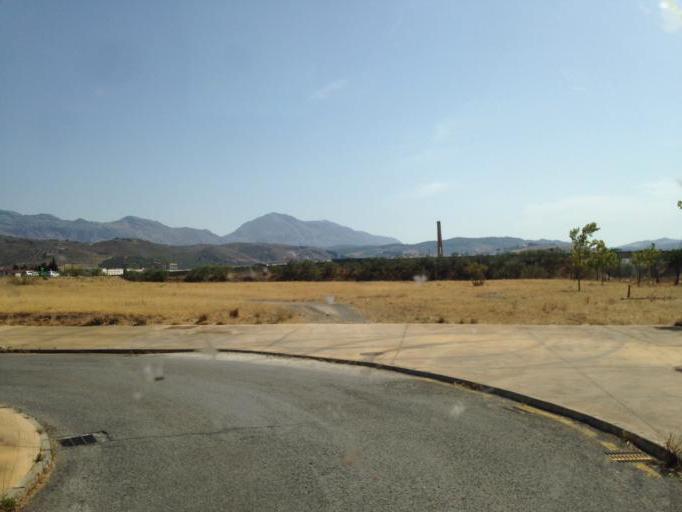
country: ES
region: Andalusia
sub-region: Provincia de Malaga
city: Antequera
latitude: 37.0367
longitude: -4.5276
